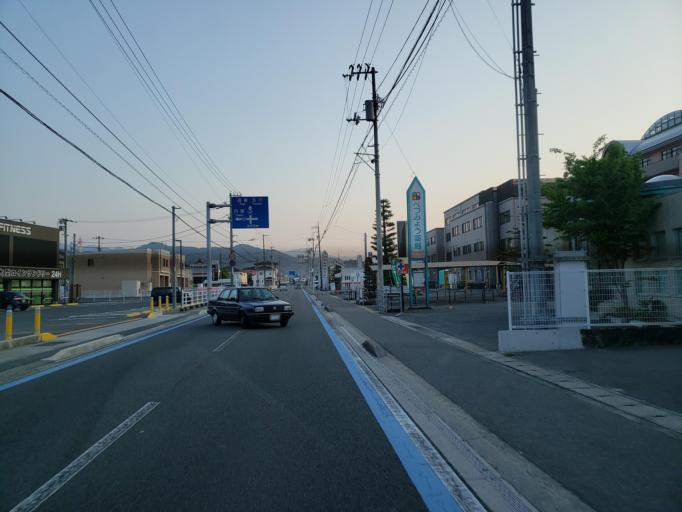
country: JP
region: Ehime
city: Hojo
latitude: 34.0424
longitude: 132.9768
